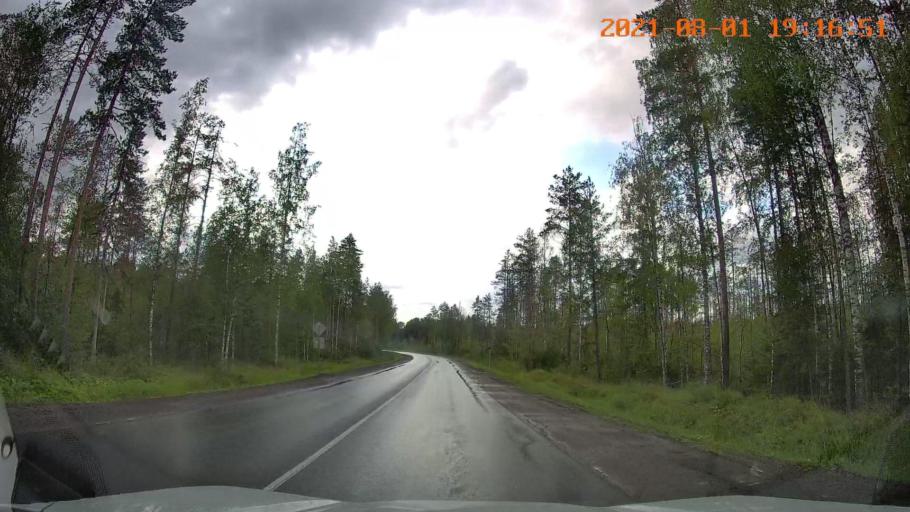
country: RU
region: Leningrad
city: Podporozh'ye
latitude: 60.8827
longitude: 34.1673
